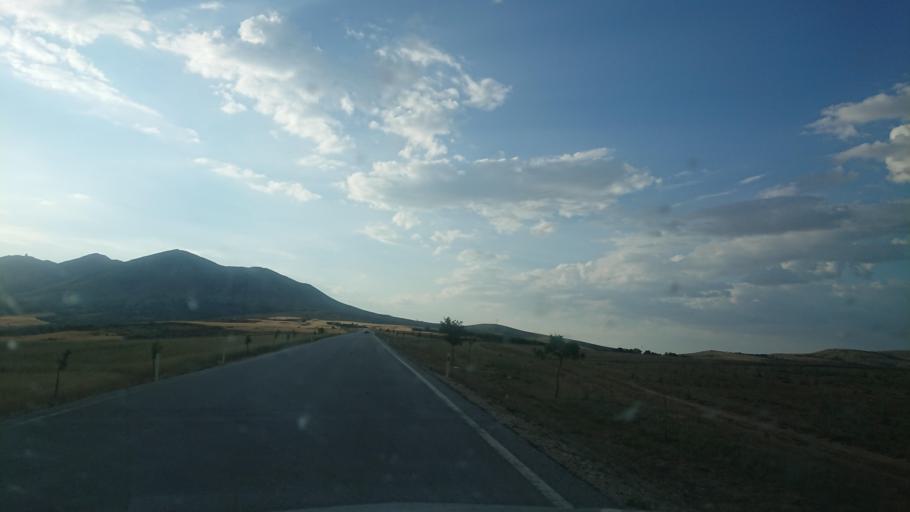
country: TR
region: Aksaray
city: Balci
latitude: 38.6135
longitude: 34.1012
